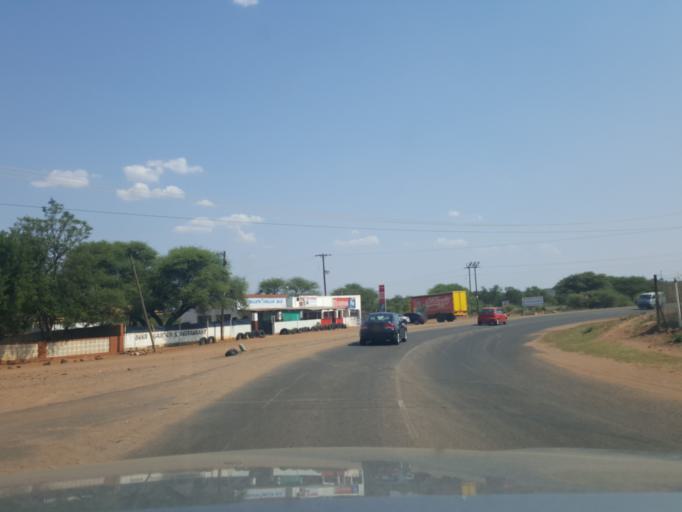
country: BW
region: South East
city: Ramotswa
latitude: -24.8485
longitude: 25.8306
